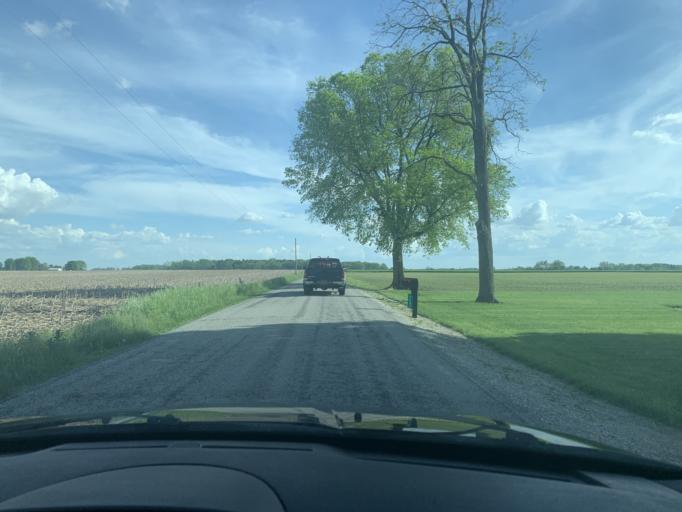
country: US
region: Ohio
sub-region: Logan County
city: De Graff
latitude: 40.2496
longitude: -84.0168
